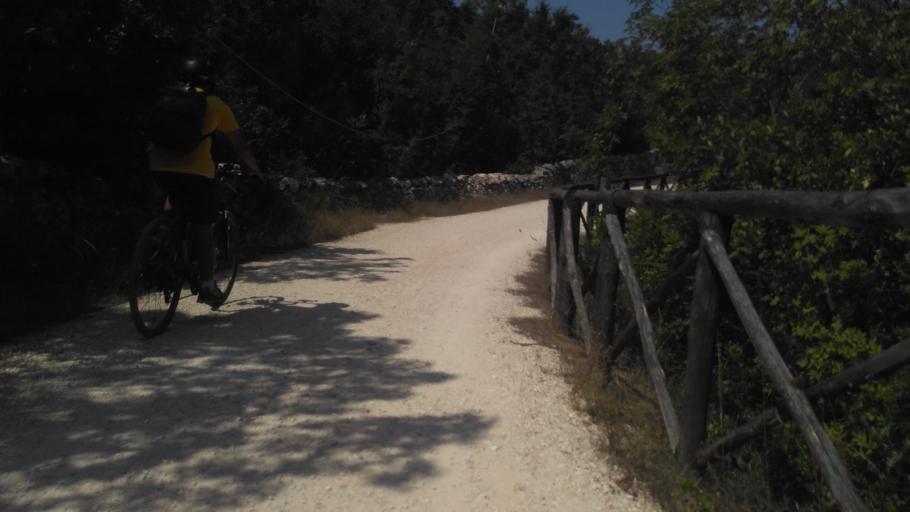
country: IT
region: Apulia
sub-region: Provincia di Brindisi
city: Cisternino
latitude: 40.6843
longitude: 17.4315
